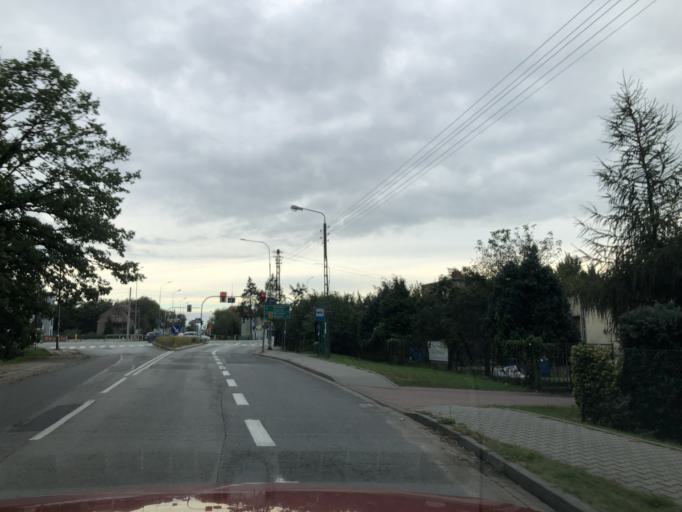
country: PL
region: Lower Silesian Voivodeship
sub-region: Powiat wroclawski
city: Dlugoleka
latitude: 51.1793
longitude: 17.1904
